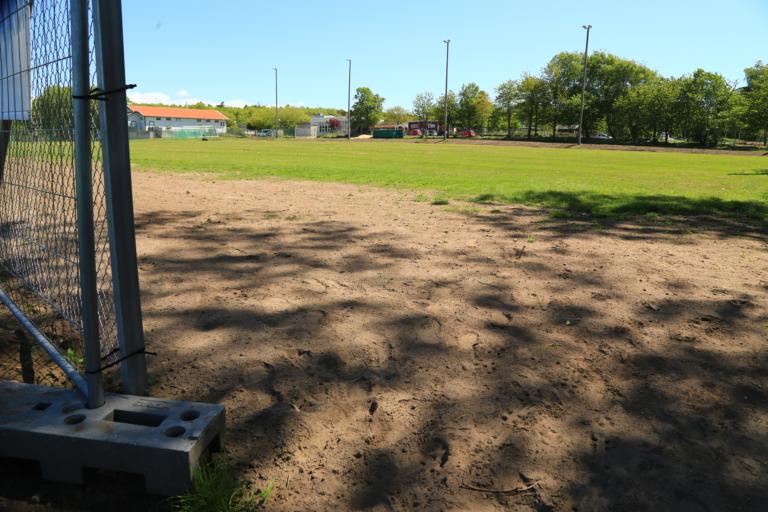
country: SE
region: Halland
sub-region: Varbergs Kommun
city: Varberg
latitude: 57.0969
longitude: 12.2626
